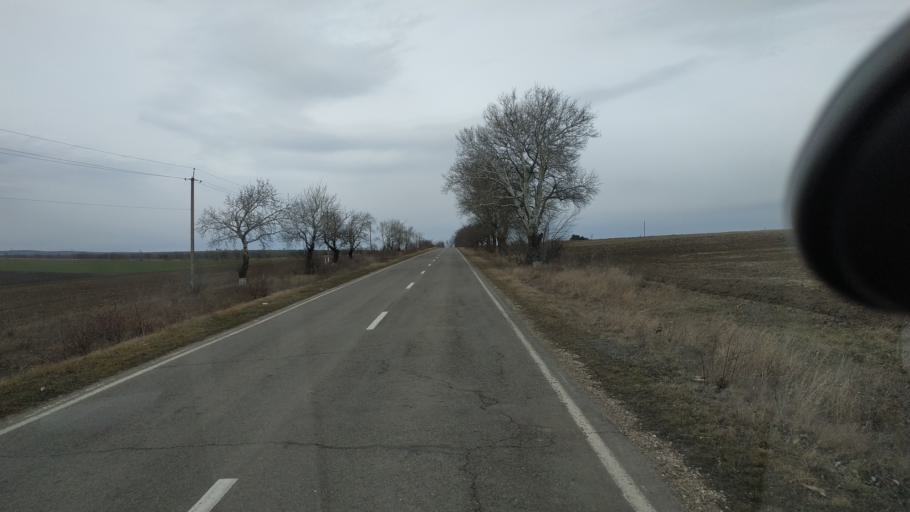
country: MD
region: Telenesti
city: Cocieri
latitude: 47.3742
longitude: 29.1104
